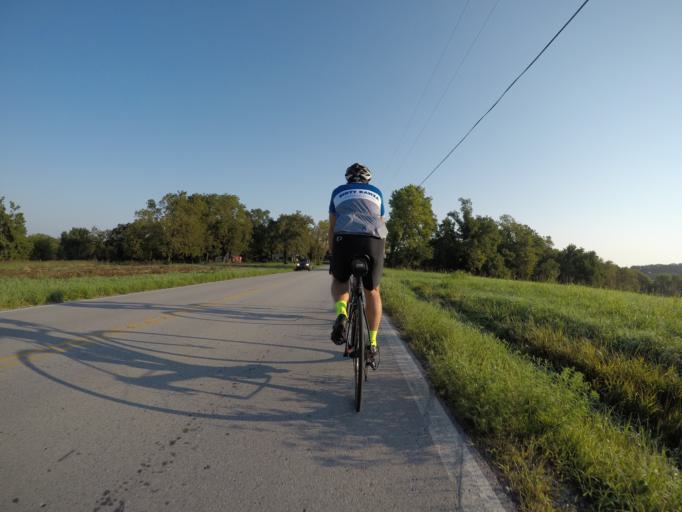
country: US
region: Kansas
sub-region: Leavenworth County
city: Lansing
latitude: 39.2435
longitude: -94.8722
